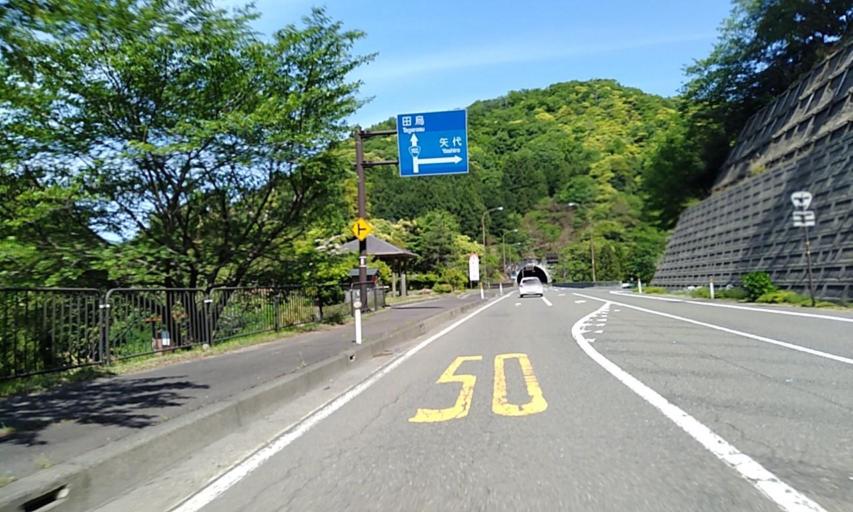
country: JP
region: Fukui
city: Obama
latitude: 35.5259
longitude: 135.8058
